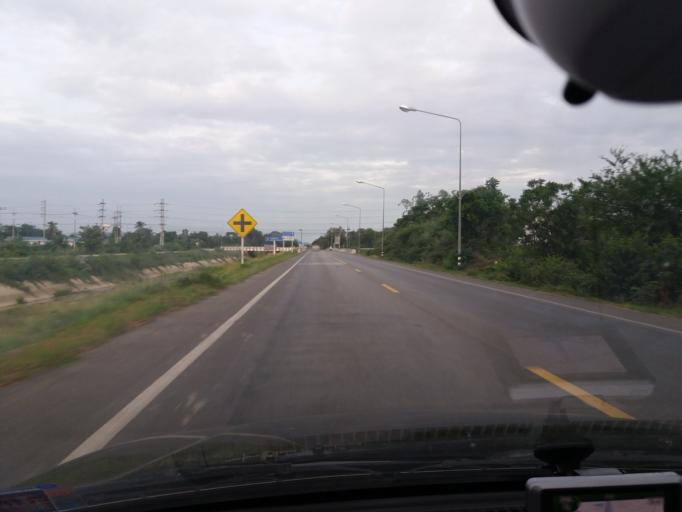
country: TH
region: Suphan Buri
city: U Thong
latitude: 14.5134
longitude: 99.9168
